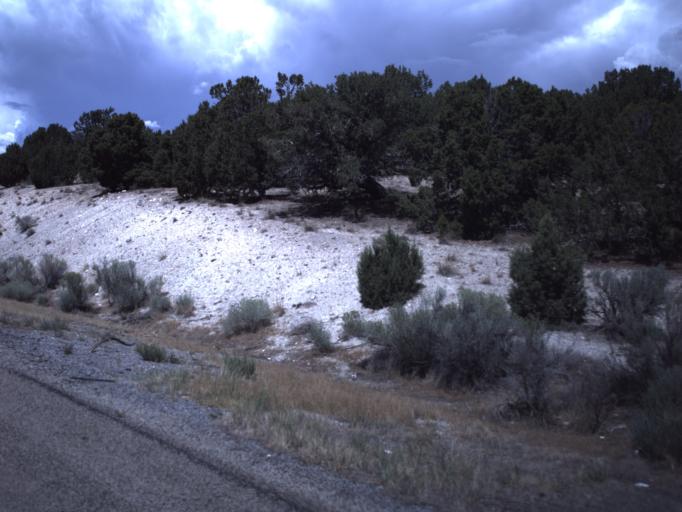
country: US
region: Utah
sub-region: Juab County
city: Nephi
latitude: 39.6661
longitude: -112.0481
